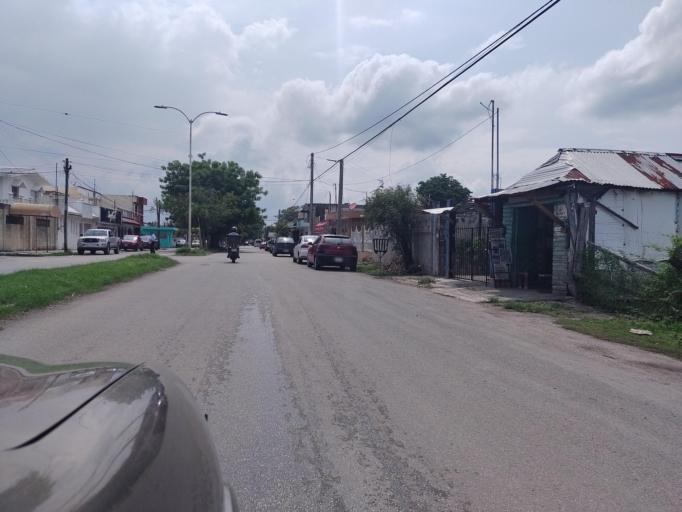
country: MX
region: Quintana Roo
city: Chetumal
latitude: 18.5166
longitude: -88.3088
